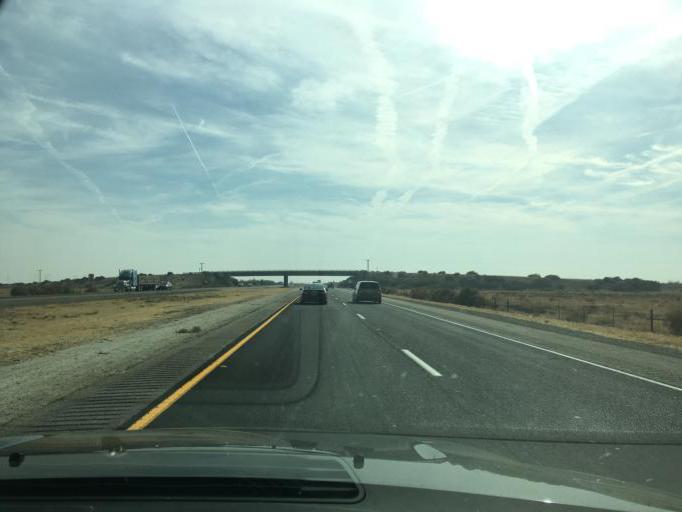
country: US
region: California
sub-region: Kern County
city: Lost Hills
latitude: 35.7921
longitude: -119.7844
